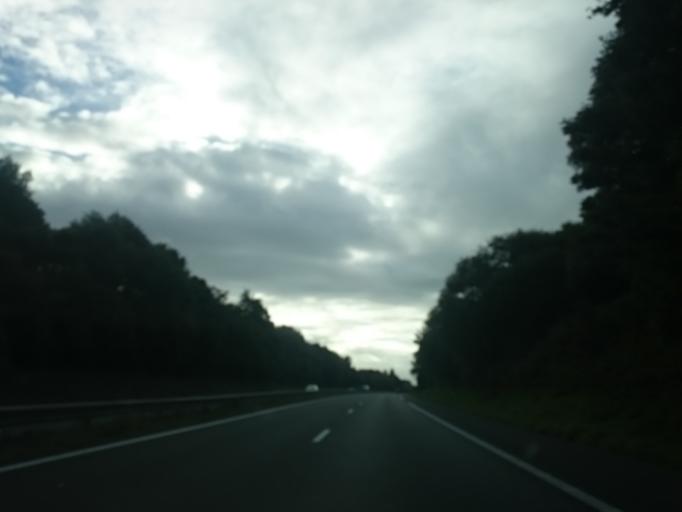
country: FR
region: Brittany
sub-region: Departement des Cotes-d'Armor
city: Belle-Isle-en-Terre
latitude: 48.5485
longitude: -3.4190
